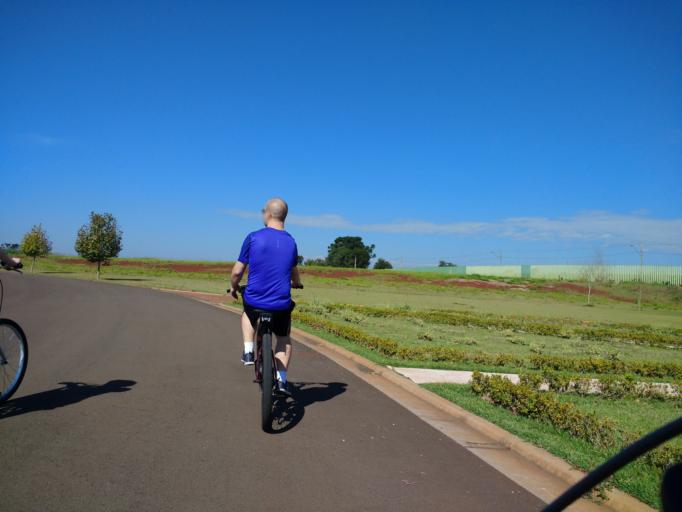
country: BR
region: Parana
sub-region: Londrina
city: Londrina
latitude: -23.3678
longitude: -51.1860
